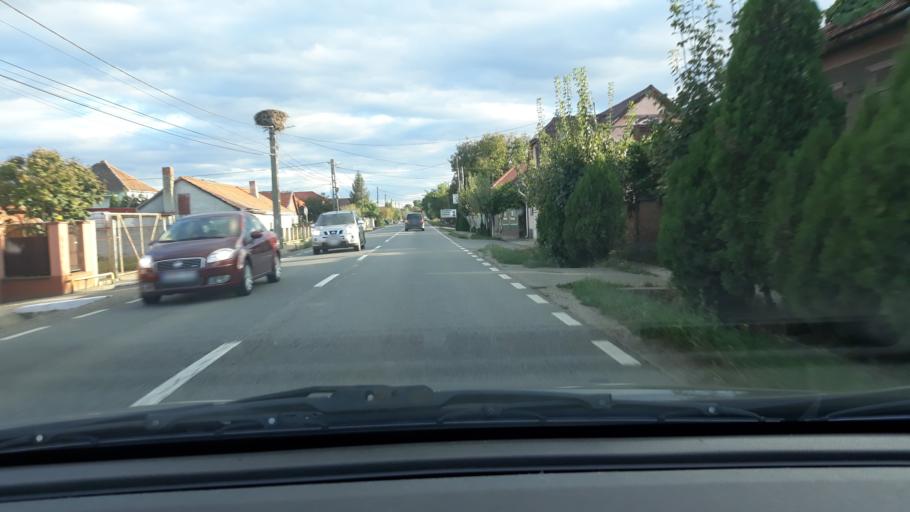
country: RO
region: Bihor
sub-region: Comuna Biharea
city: Biharea
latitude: 47.1652
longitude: 21.9221
